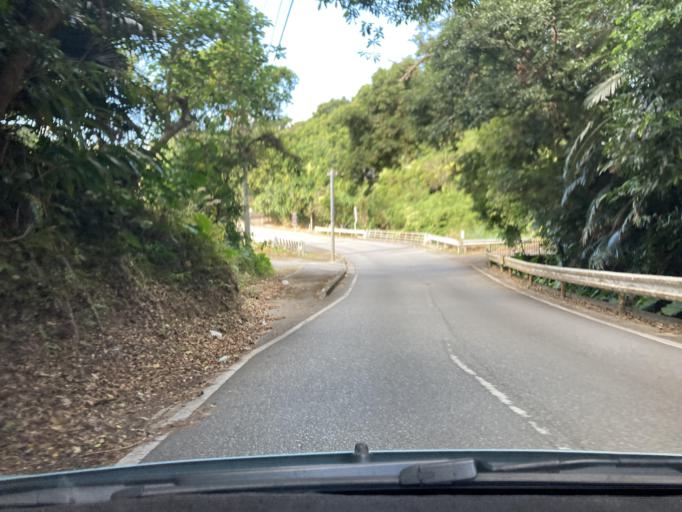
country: JP
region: Okinawa
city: Gushikawa
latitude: 26.3756
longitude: 127.8299
